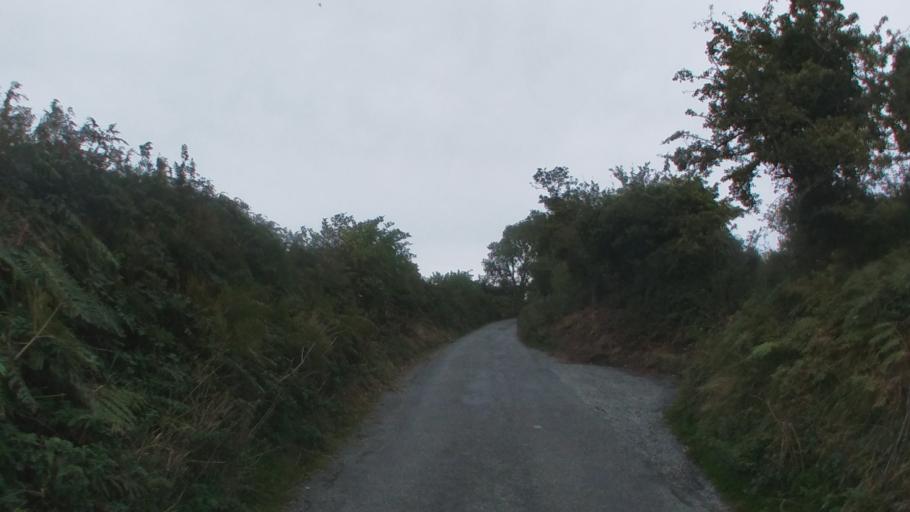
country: IE
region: Leinster
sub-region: Wicklow
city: Enniskerry
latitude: 53.1836
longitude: -6.2078
